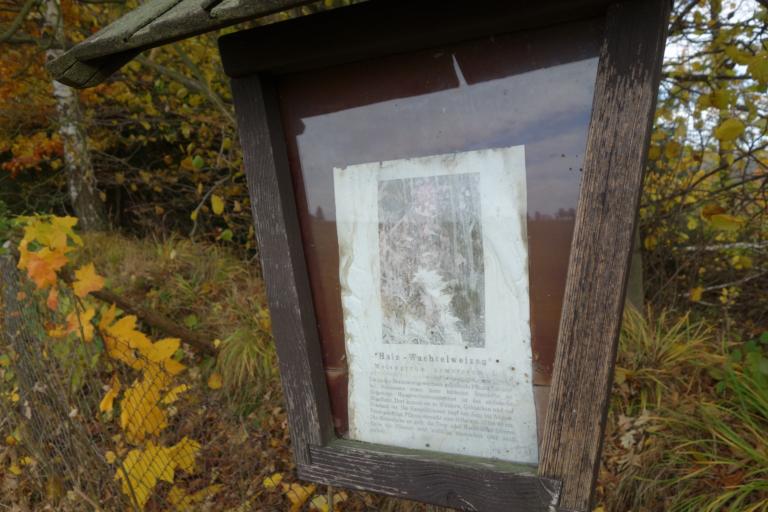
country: DE
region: Saxony
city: Neuhausen
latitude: 50.6862
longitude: 13.4556
